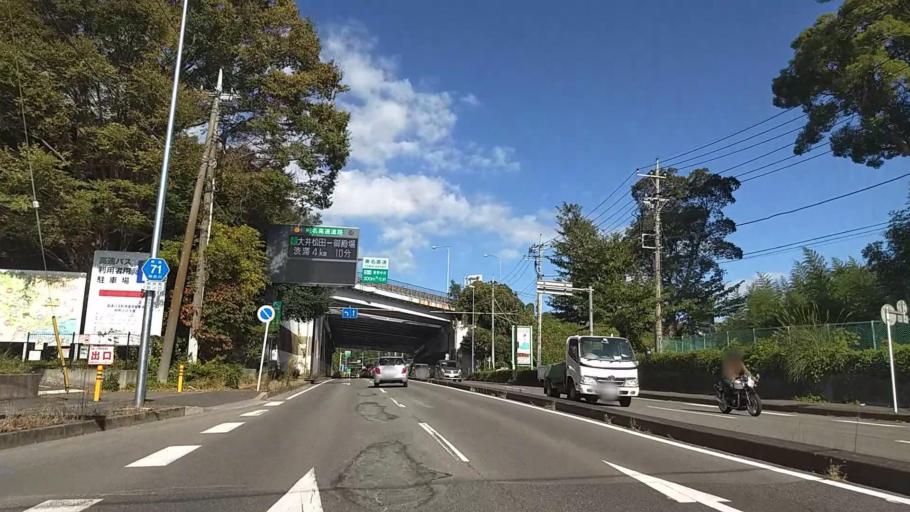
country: JP
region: Kanagawa
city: Hadano
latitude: 35.3521
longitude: 139.2359
